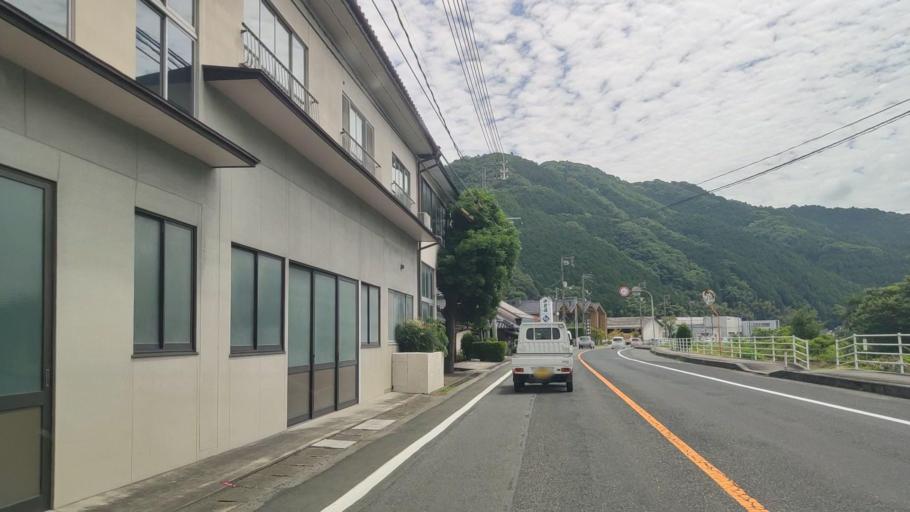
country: JP
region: Okayama
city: Niimi
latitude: 35.0839
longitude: 133.6980
